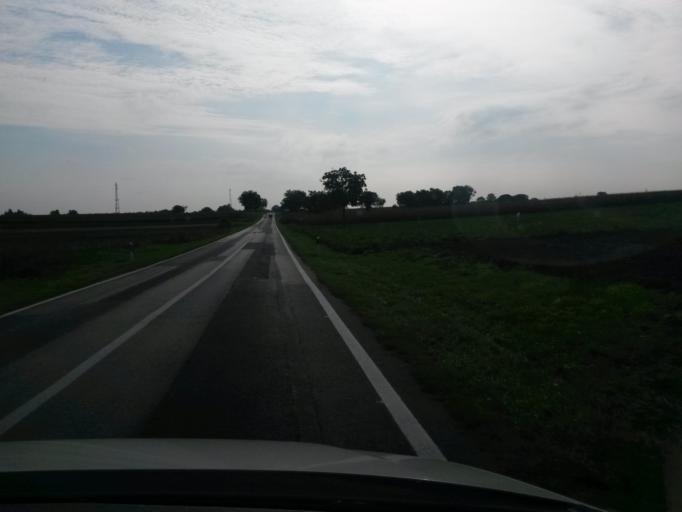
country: HR
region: Vukovarsko-Srijemska
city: Lovas
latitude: 45.2664
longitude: 19.1554
